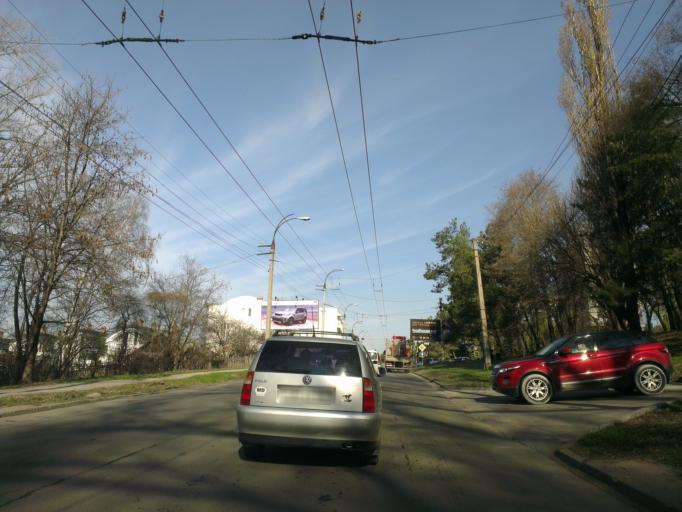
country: MD
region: Chisinau
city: Chisinau
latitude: 47.0375
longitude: 28.8599
